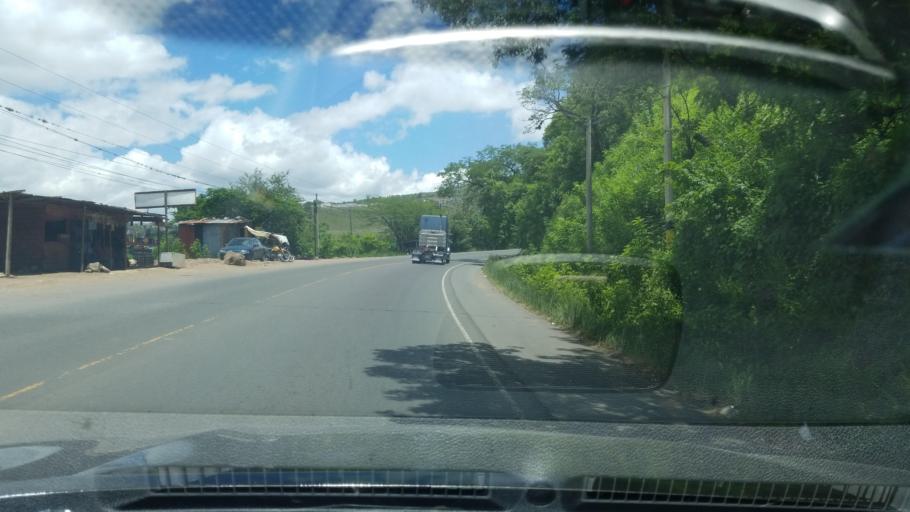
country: HN
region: Francisco Morazan
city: Rio Abajo
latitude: 14.1461
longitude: -87.2148
